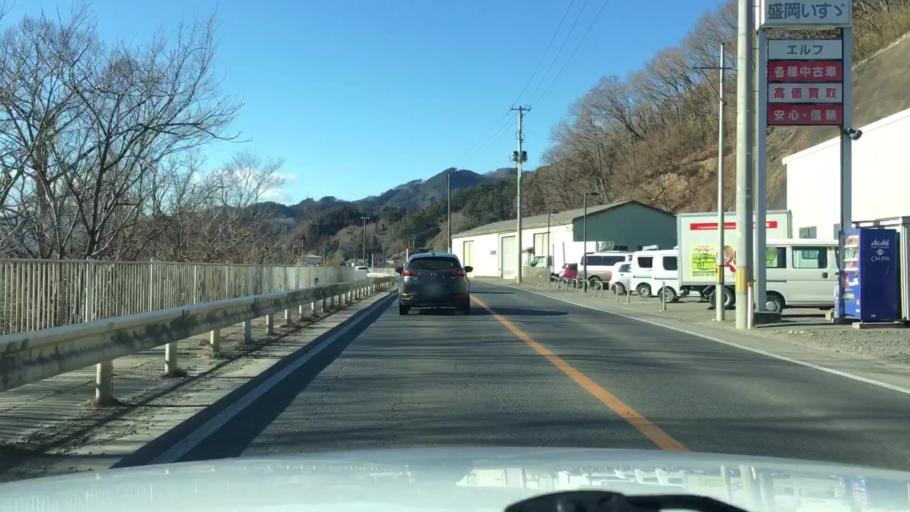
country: JP
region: Iwate
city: Miyako
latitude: 39.6325
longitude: 141.9017
